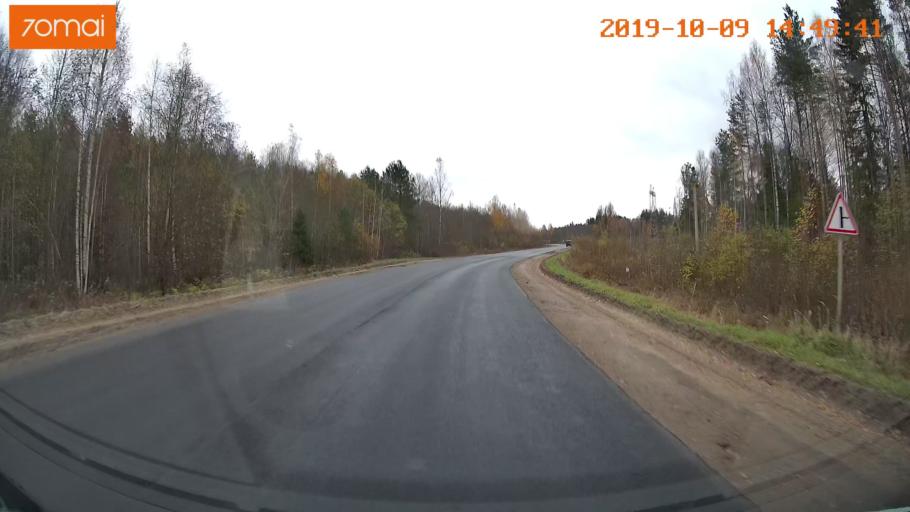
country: RU
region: Kostroma
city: Chistyye Bory
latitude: 58.3909
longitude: 41.5862
